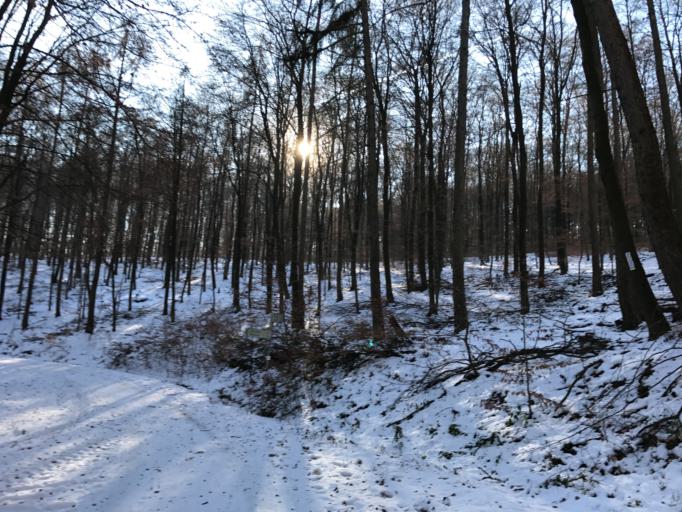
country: DE
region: Hesse
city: Eppstein
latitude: 50.1239
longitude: 8.3920
